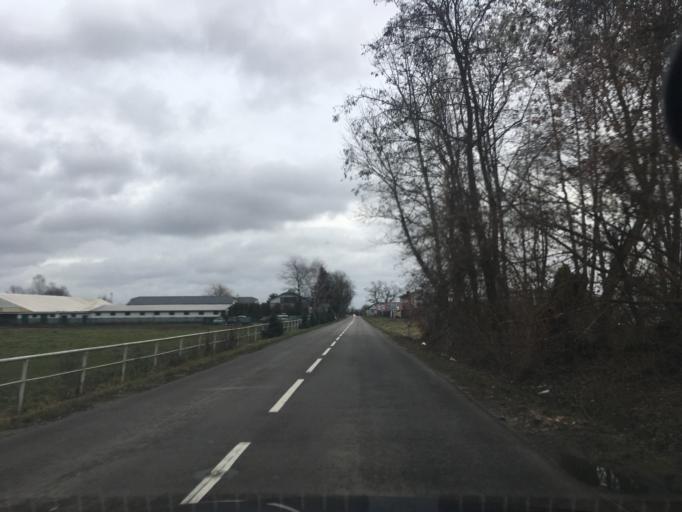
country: PL
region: Masovian Voivodeship
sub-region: Powiat piaseczynski
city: Lesznowola
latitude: 52.1203
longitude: 20.9381
